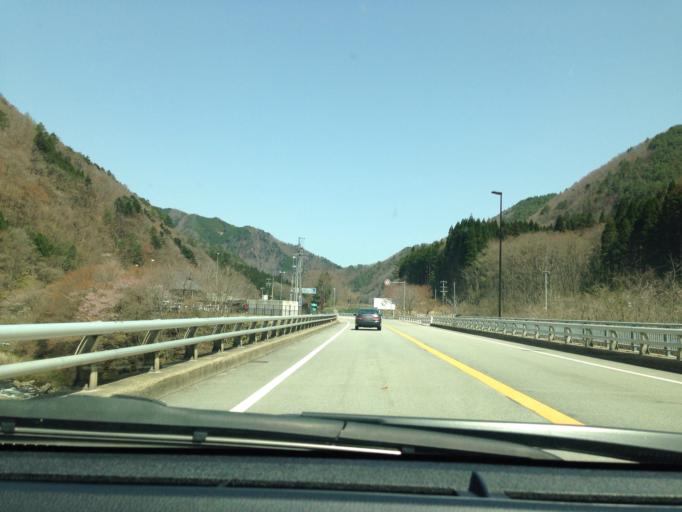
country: JP
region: Gifu
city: Takayama
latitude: 36.0047
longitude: 137.2923
